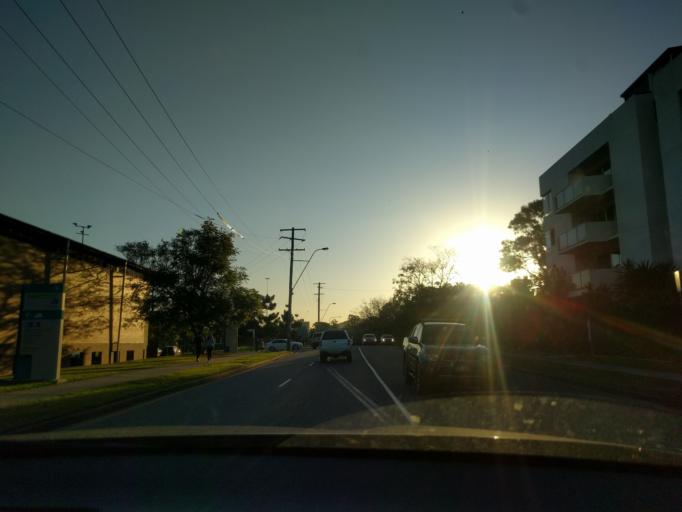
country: AU
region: Queensland
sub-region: Brisbane
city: South Brisbane
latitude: -27.4942
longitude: 153.0089
